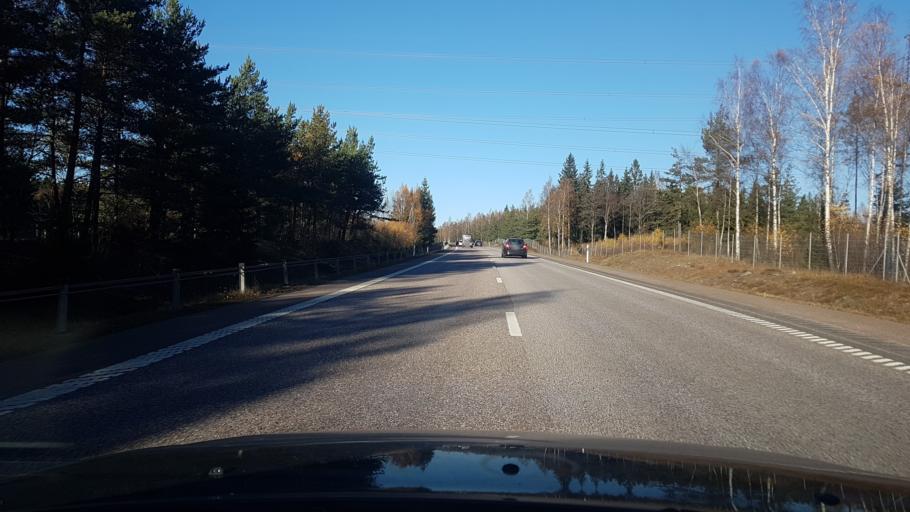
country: SE
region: Stockholm
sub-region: Sigtuna Kommun
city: Marsta
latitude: 59.6918
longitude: 17.8683
